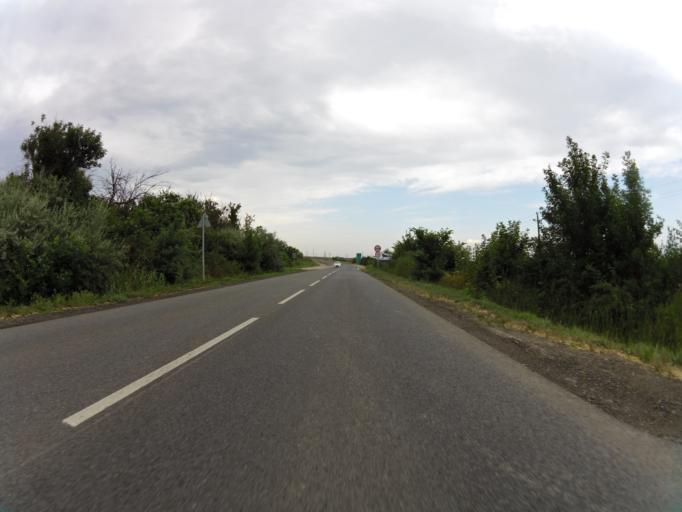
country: HU
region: Csongrad
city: Szeged
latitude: 46.2897
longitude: 20.1387
